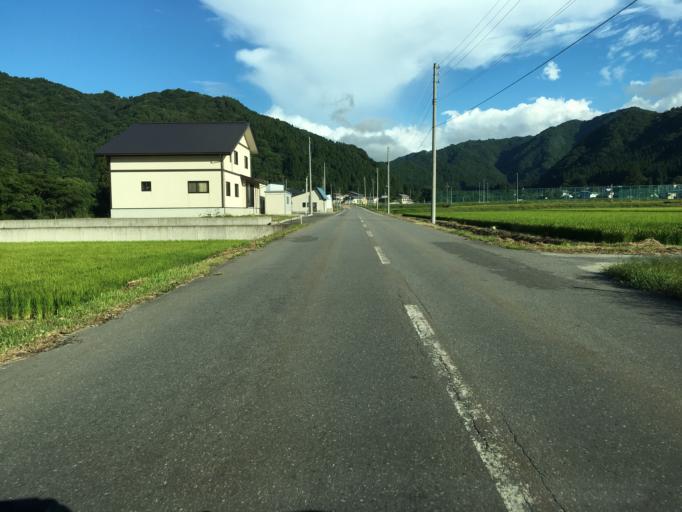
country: JP
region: Yamagata
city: Yonezawa
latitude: 37.8682
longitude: 140.1472
